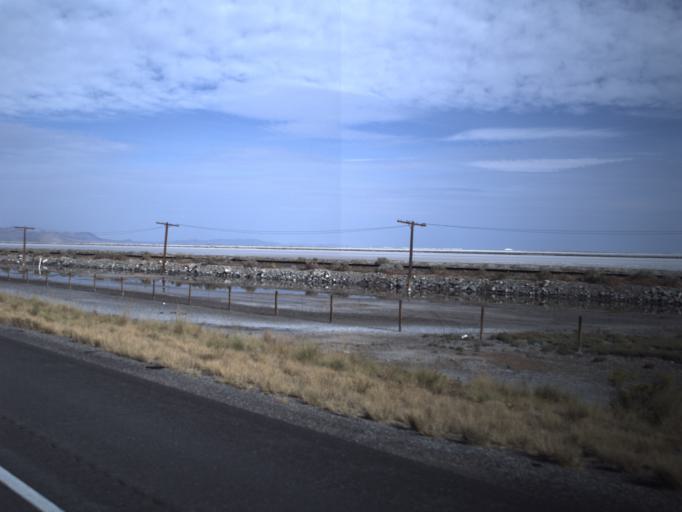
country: US
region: Utah
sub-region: Tooele County
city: Grantsville
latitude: 40.7201
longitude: -112.5538
